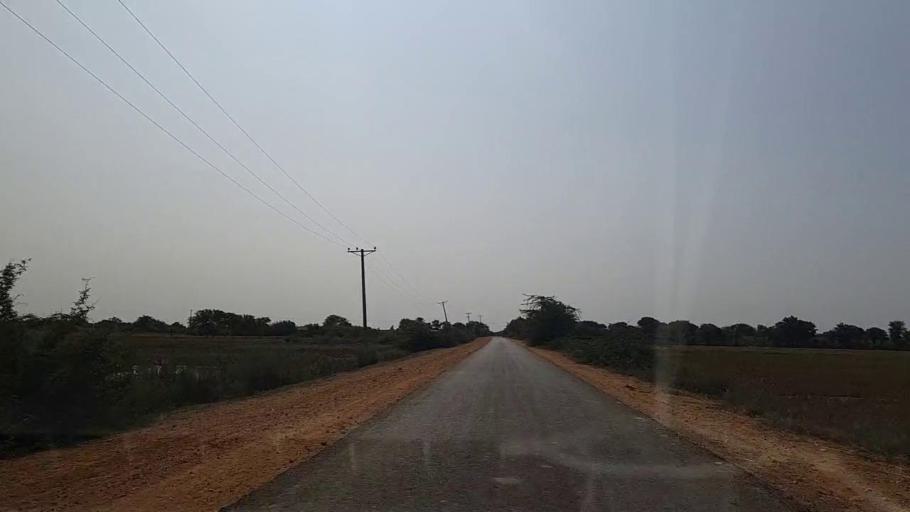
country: PK
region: Sindh
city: Chuhar Jamali
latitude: 24.3261
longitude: 67.9428
